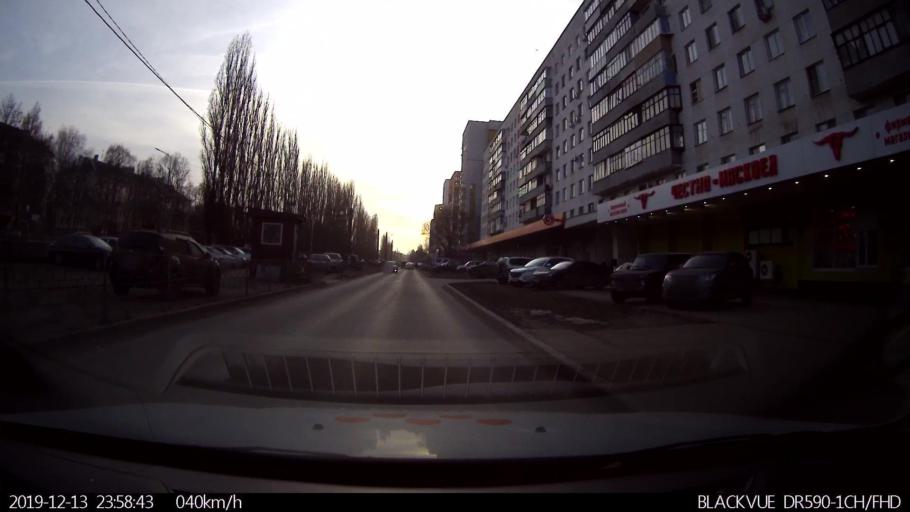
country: RU
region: Nizjnij Novgorod
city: Nizhniy Novgorod
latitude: 56.2742
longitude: 43.9190
